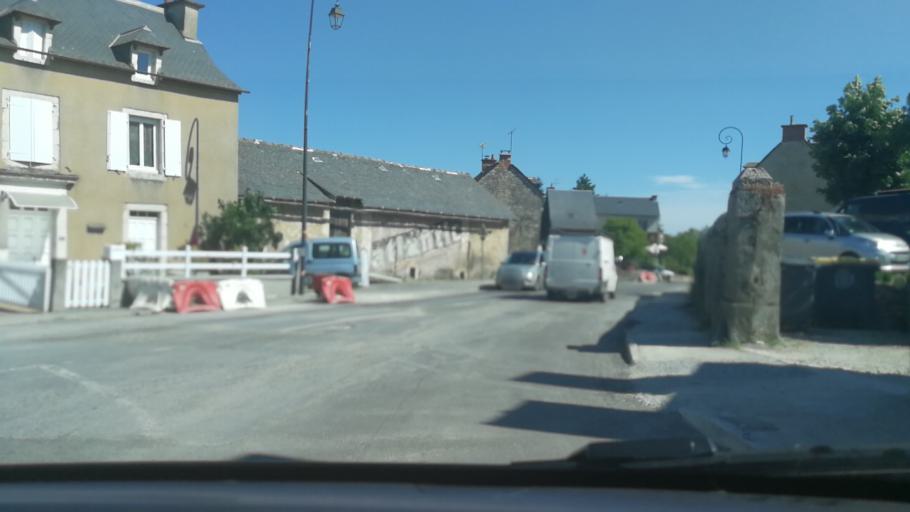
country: FR
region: Midi-Pyrenees
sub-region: Departement de l'Aveyron
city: Sebazac-Concoures
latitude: 44.4051
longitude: 2.5994
